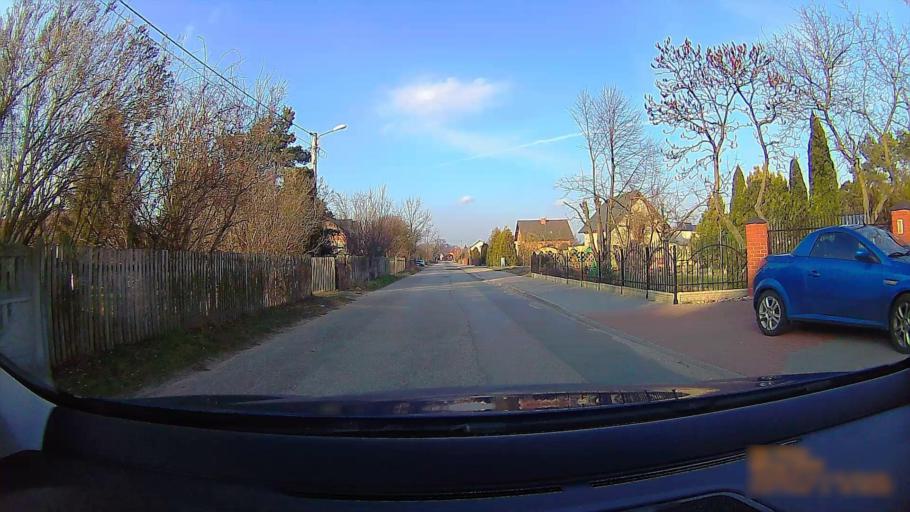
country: PL
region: Greater Poland Voivodeship
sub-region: Konin
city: Konin
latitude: 52.1859
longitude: 18.3016
